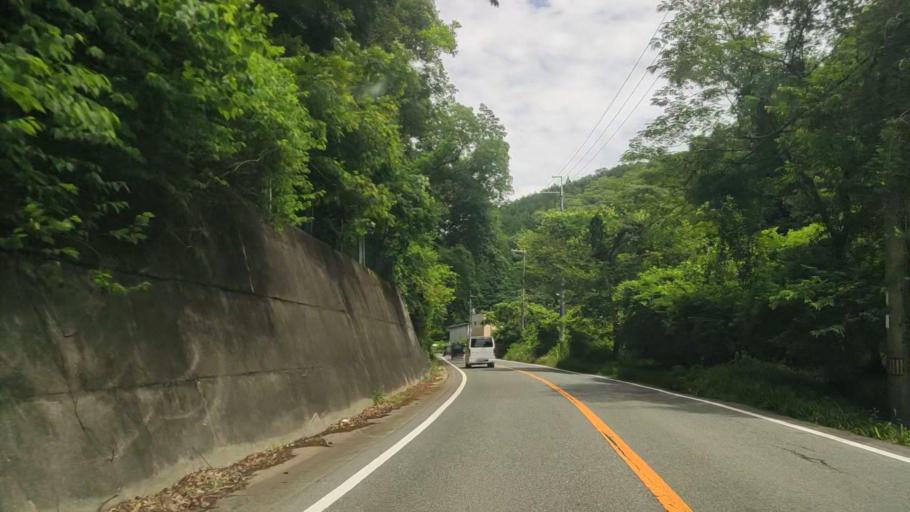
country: JP
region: Hyogo
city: Yamazakicho-nakabirose
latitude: 34.9914
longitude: 134.4038
